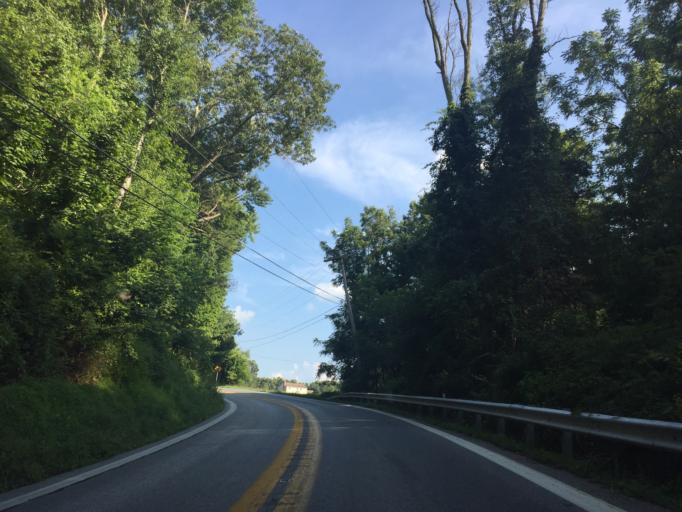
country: US
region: Maryland
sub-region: Carroll County
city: Hampstead
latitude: 39.6135
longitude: -76.7895
